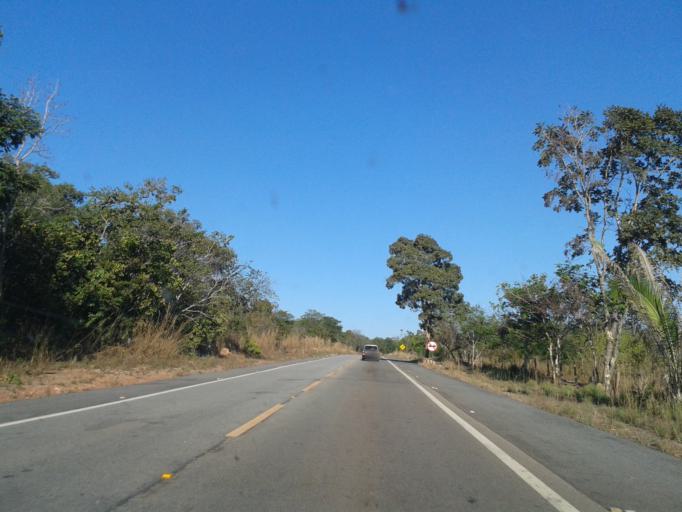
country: BR
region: Goias
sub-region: Mozarlandia
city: Mozarlandia
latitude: -15.1828
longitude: -50.5554
